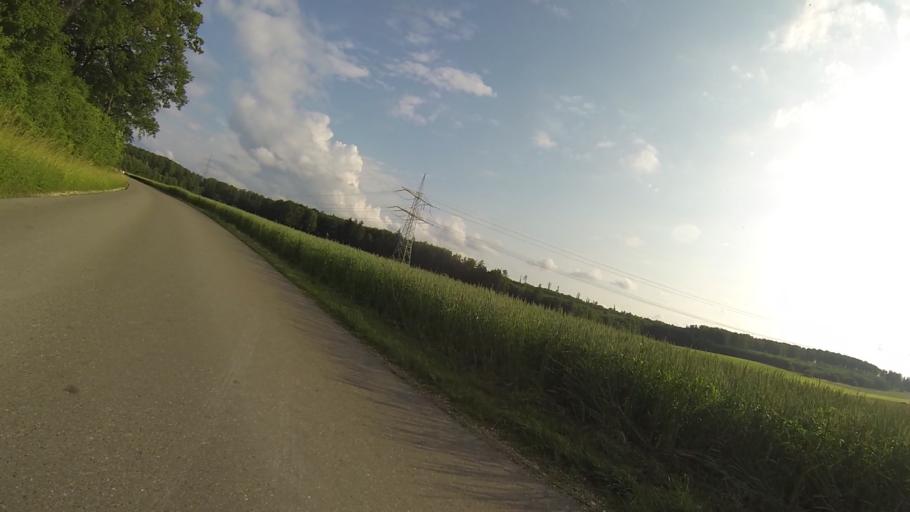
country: DE
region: Baden-Wuerttemberg
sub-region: Regierungsbezirk Stuttgart
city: Nattheim
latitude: 48.7302
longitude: 10.2450
